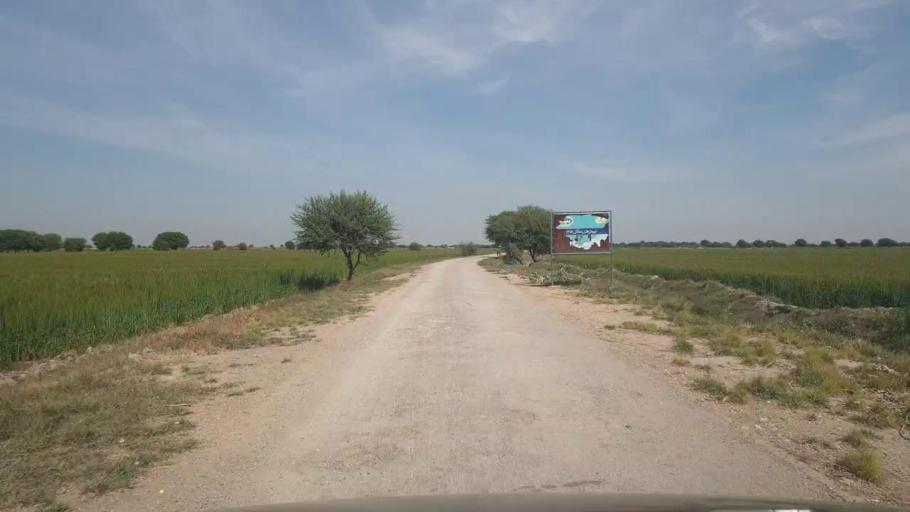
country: PK
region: Sindh
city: Kunri
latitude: 25.2190
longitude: 69.6462
